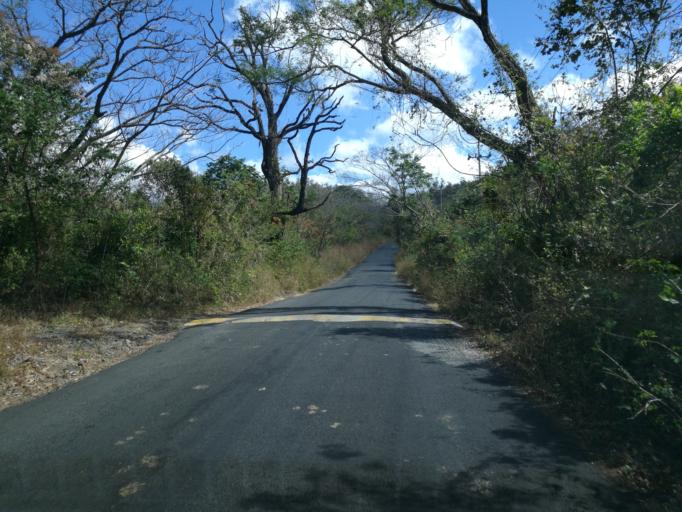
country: CR
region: Guanacaste
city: Liberia
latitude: 10.7348
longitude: -85.3883
